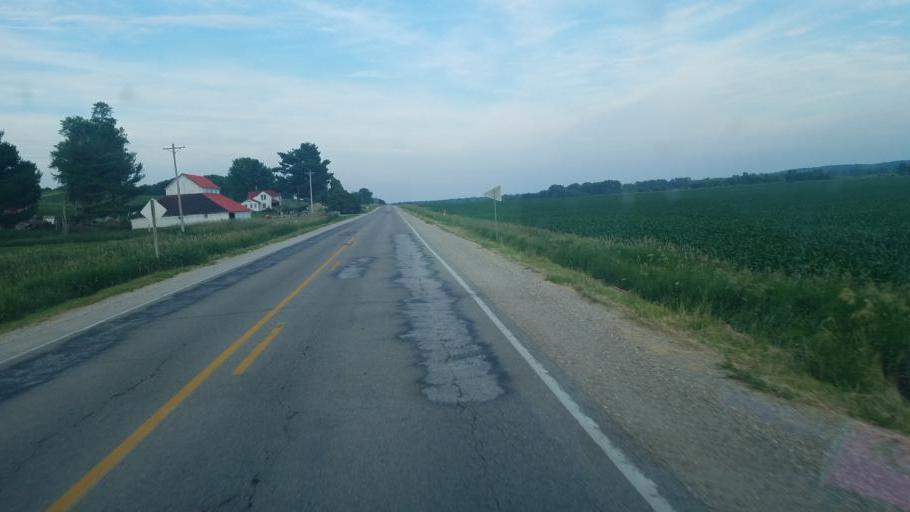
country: US
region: Iowa
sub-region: Benton County
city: Belle Plaine
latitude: 41.9111
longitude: -92.3451
